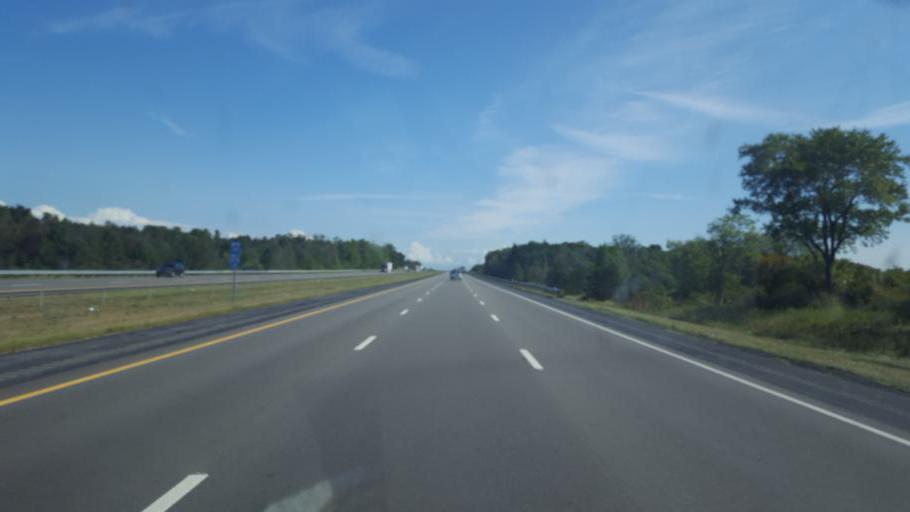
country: US
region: Ohio
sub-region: Medina County
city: Medina
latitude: 41.0808
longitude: -81.8371
